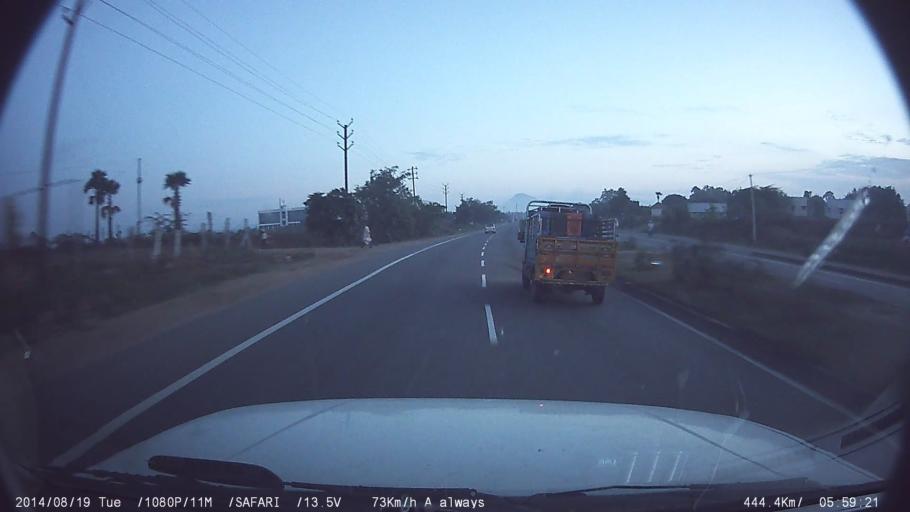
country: IN
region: Tamil Nadu
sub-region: Salem
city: Omalur
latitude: 11.7933
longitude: 78.0569
